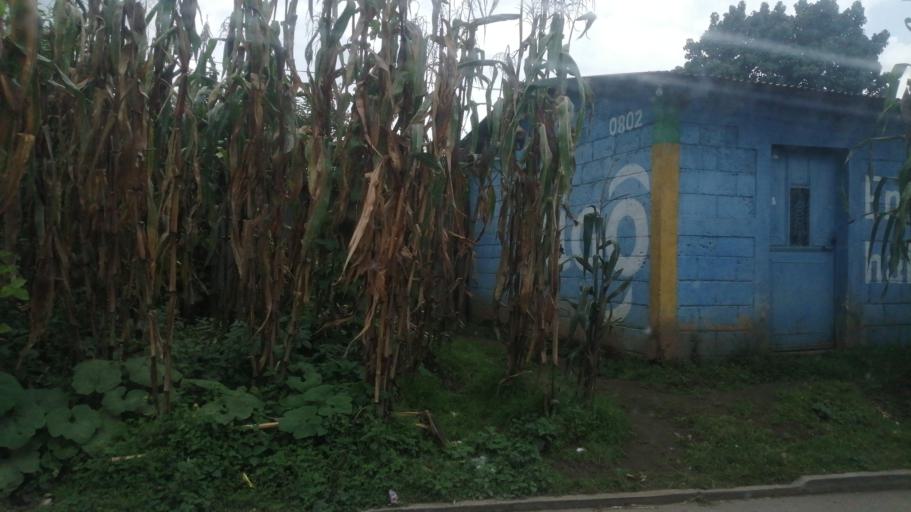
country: GT
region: Quetzaltenango
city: Cantel
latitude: 14.8181
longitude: -91.4405
